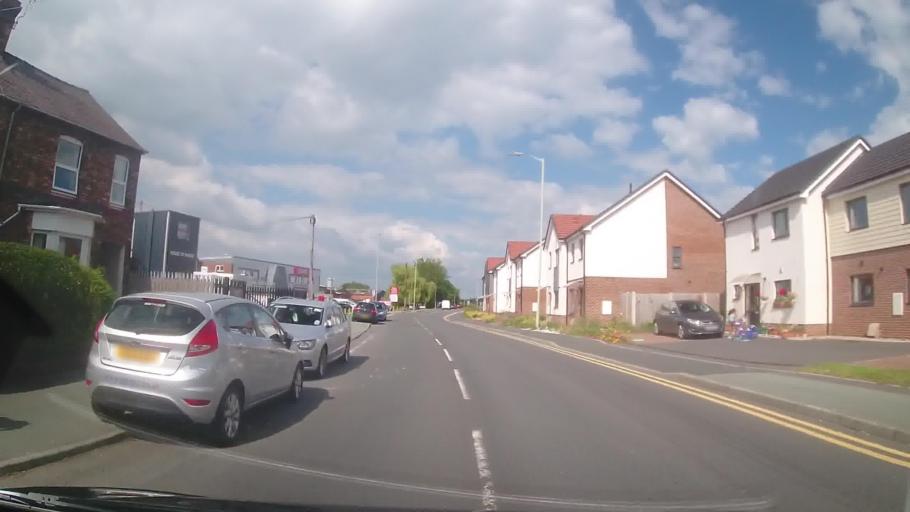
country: GB
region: England
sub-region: Shropshire
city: Oswestry
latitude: 52.8660
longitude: -3.0429
